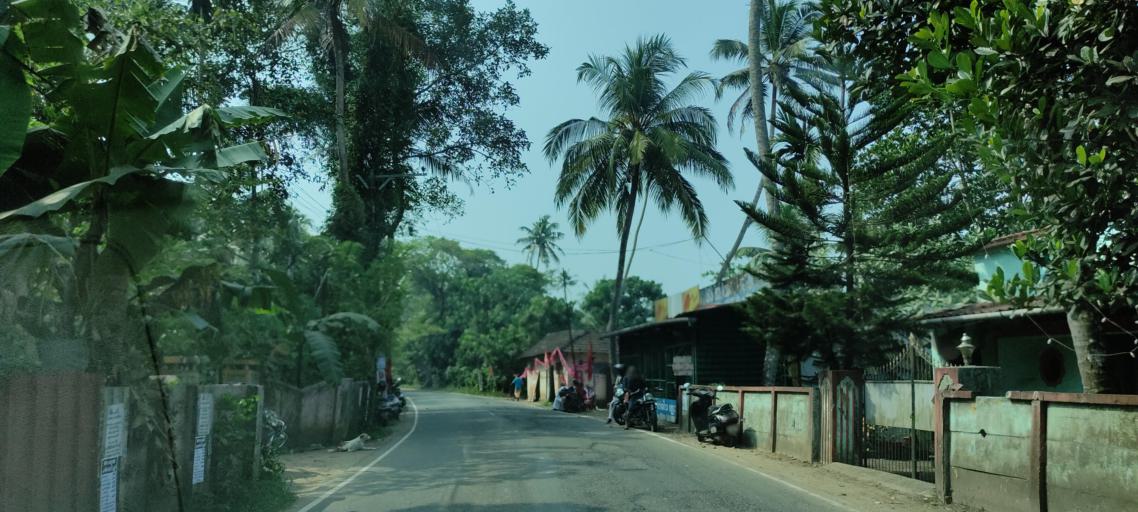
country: IN
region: Kerala
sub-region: Kottayam
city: Vaikam
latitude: 9.7395
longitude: 76.4069
